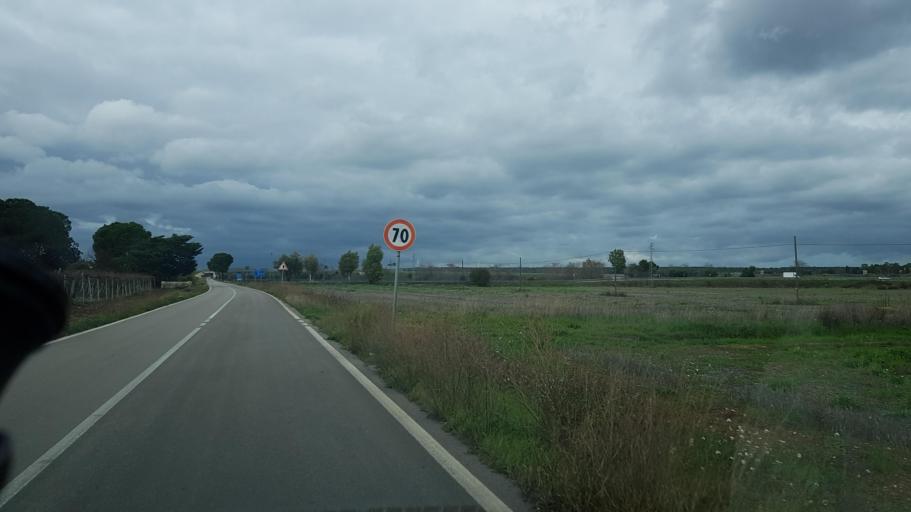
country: IT
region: Apulia
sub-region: Provincia di Brindisi
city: Francavilla Fontana
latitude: 40.5438
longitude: 17.5580
